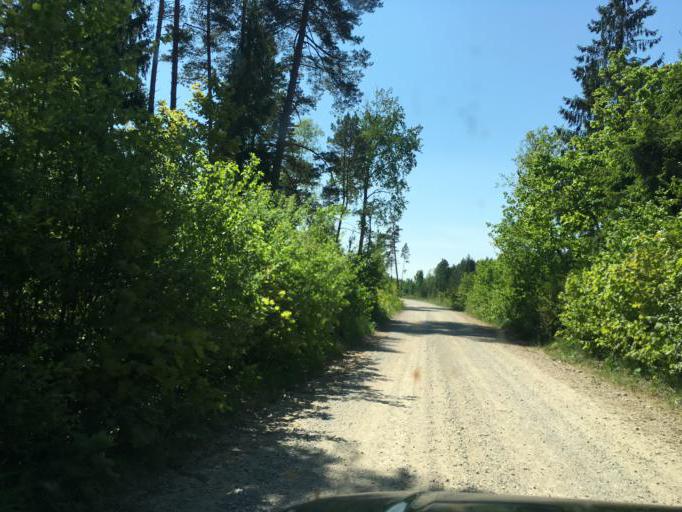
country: LV
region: Rojas
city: Roja
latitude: 57.4241
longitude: 22.7132
